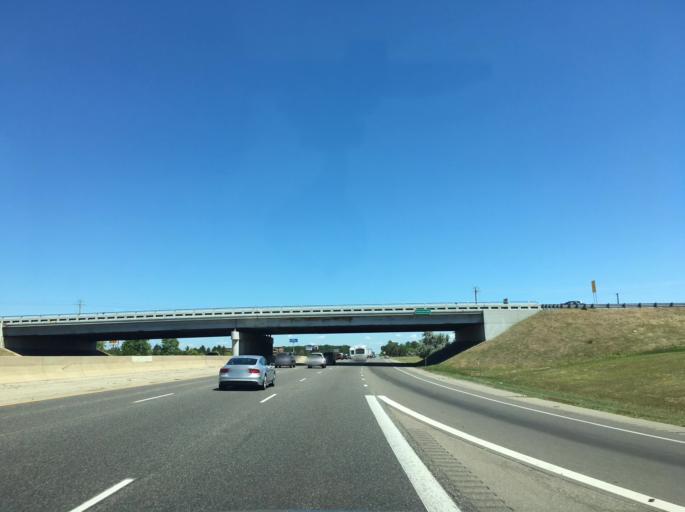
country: US
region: Michigan
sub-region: Genesee County
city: Beecher
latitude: 43.0597
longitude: -83.7622
